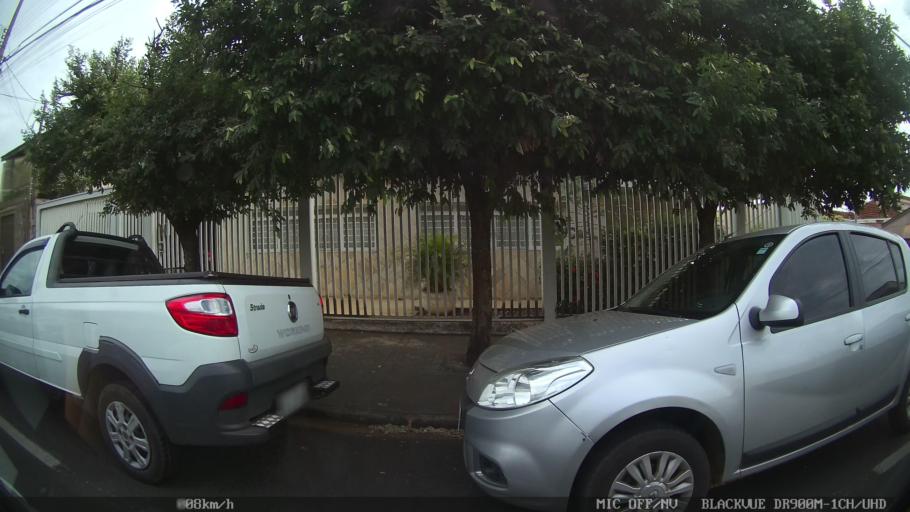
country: BR
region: Sao Paulo
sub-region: Sao Jose Do Rio Preto
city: Sao Jose do Rio Preto
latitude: -20.8153
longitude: -49.3719
